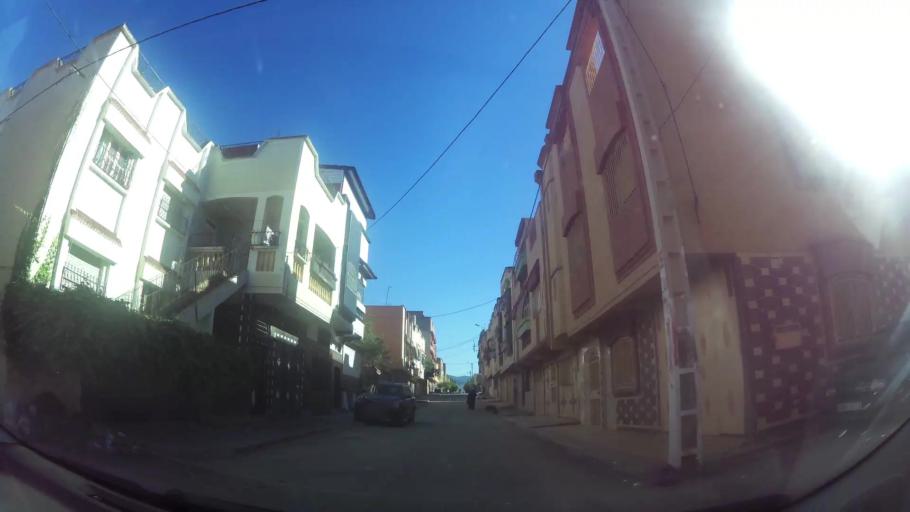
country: MA
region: Oriental
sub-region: Berkane-Taourirt
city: Ahfir
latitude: 34.9579
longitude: -2.0983
